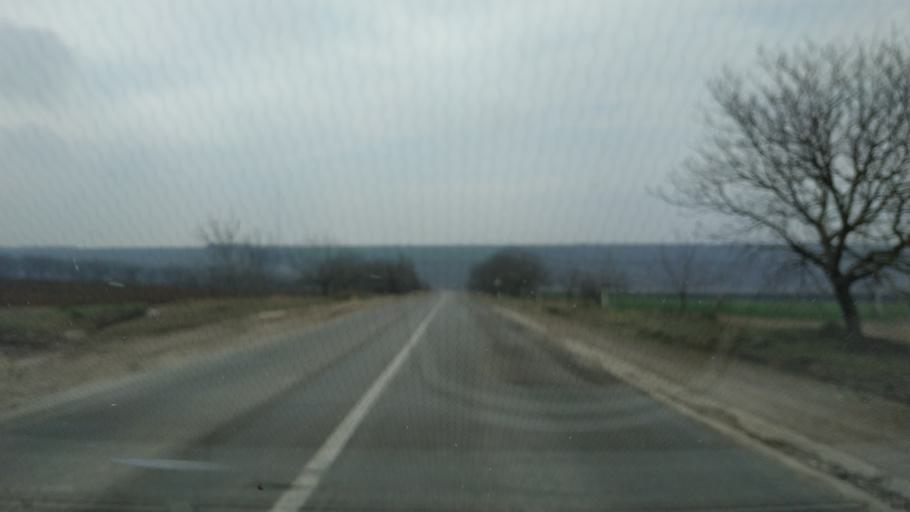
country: MD
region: Cahul
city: Cahul
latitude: 45.9460
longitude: 28.3068
